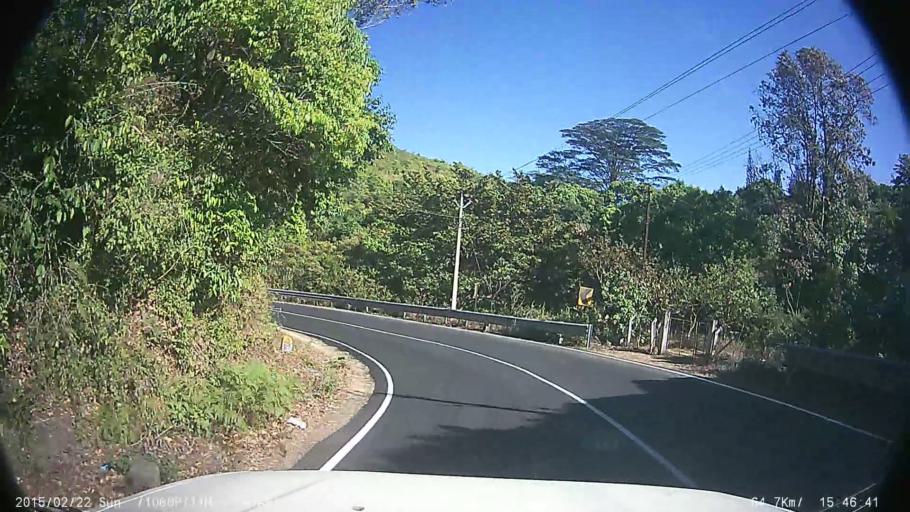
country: IN
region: Kerala
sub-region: Kottayam
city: Erattupetta
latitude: 9.5786
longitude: 76.9851
